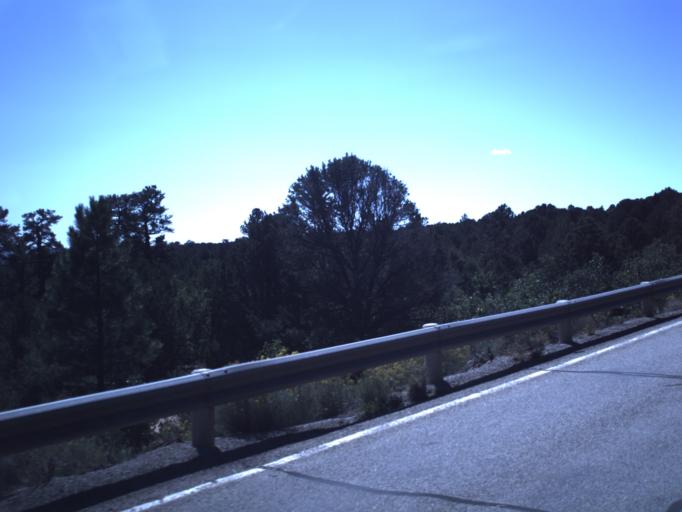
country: US
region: Utah
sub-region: Grand County
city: Moab
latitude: 38.3324
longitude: -109.2189
